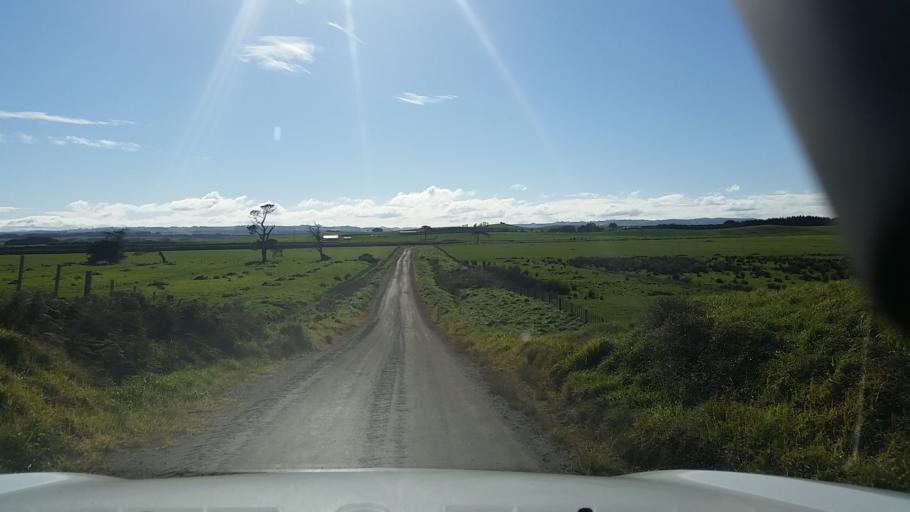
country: NZ
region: Taranaki
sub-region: South Taranaki District
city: Patea
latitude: -39.7782
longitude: 174.5478
